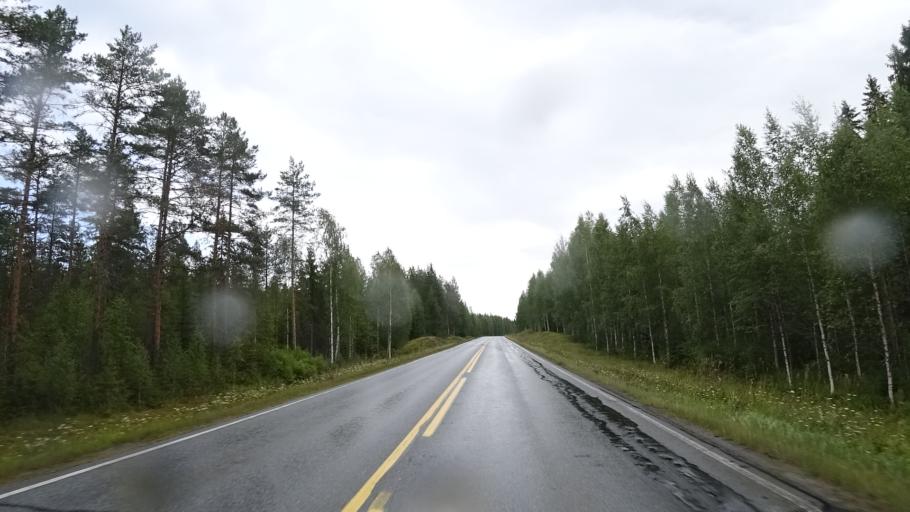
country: FI
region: North Karelia
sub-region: Keski-Karjala
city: Kesaelahti
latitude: 62.1073
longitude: 29.7941
